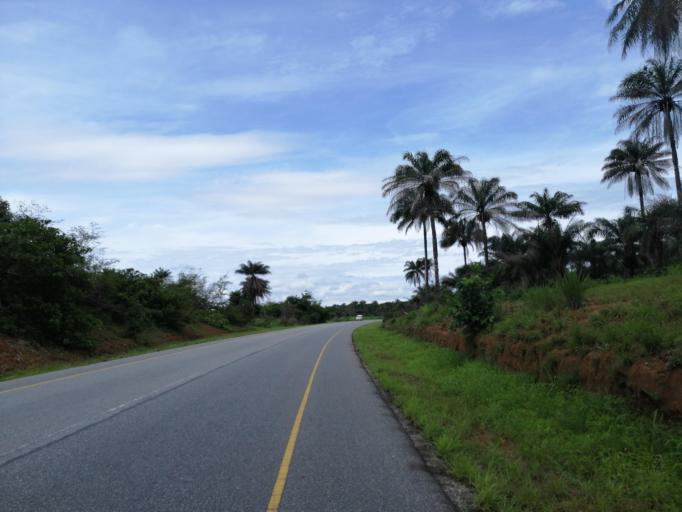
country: SL
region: Northern Province
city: Port Loko
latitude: 8.7511
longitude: -12.9182
